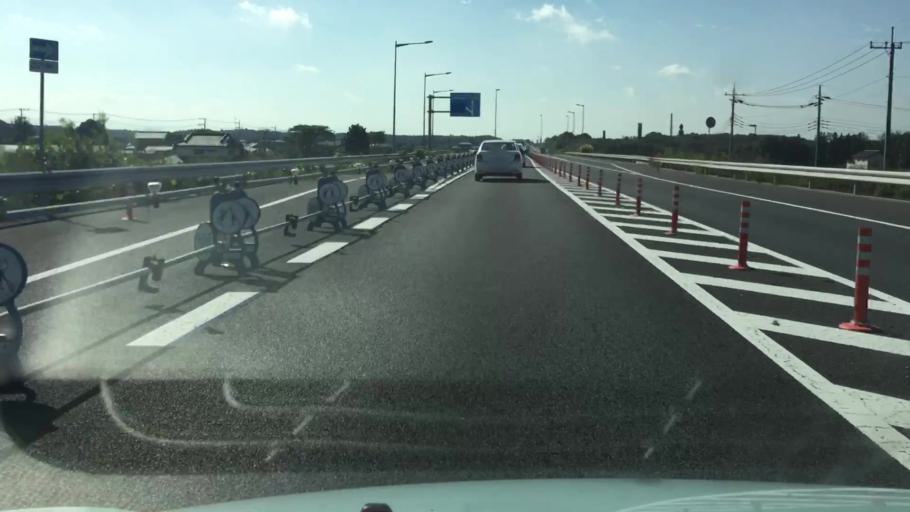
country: JP
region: Tochigi
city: Mooka
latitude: 36.5158
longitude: 139.9862
